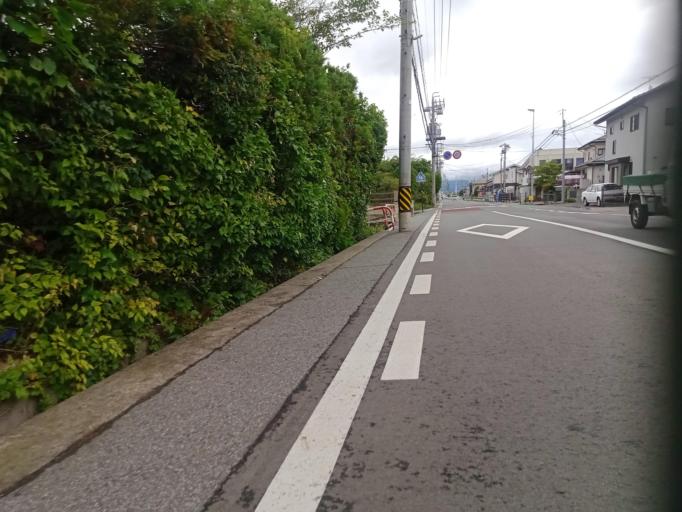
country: JP
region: Nagano
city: Nagano-shi
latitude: 36.6279
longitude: 138.1643
